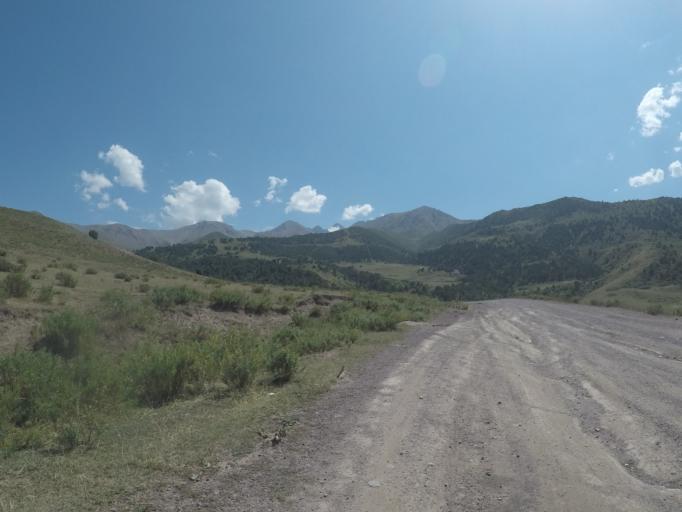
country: KG
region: Chuy
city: Bishkek
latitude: 42.6478
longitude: 74.5169
